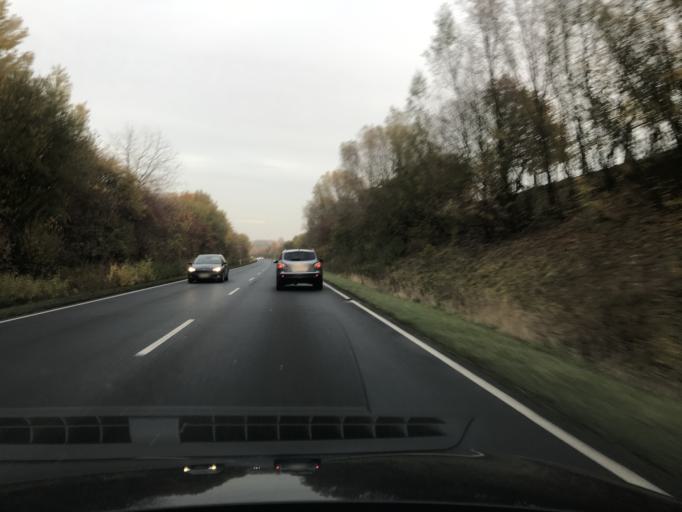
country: DE
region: North Rhine-Westphalia
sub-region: Regierungsbezirk Arnsberg
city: Hamm
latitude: 51.7049
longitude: 7.7366
